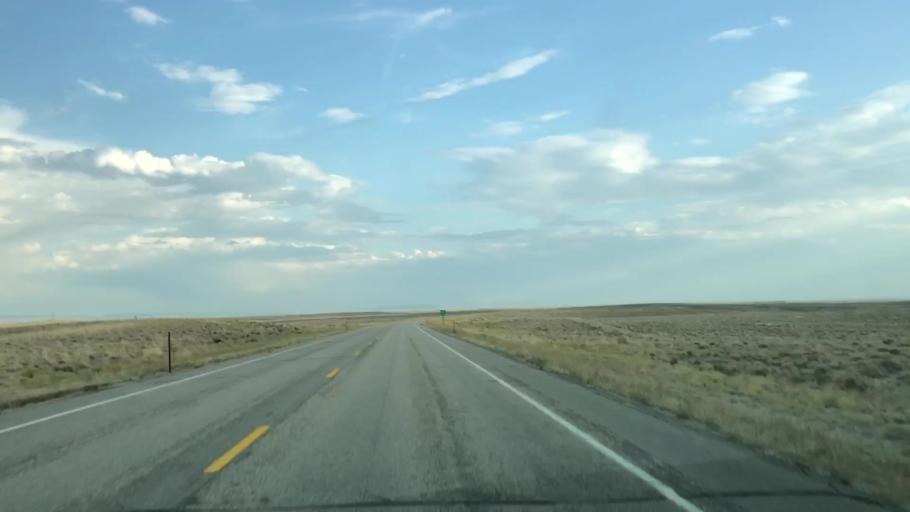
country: US
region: Wyoming
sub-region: Sweetwater County
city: North Rock Springs
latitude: 42.2592
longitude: -109.4711
